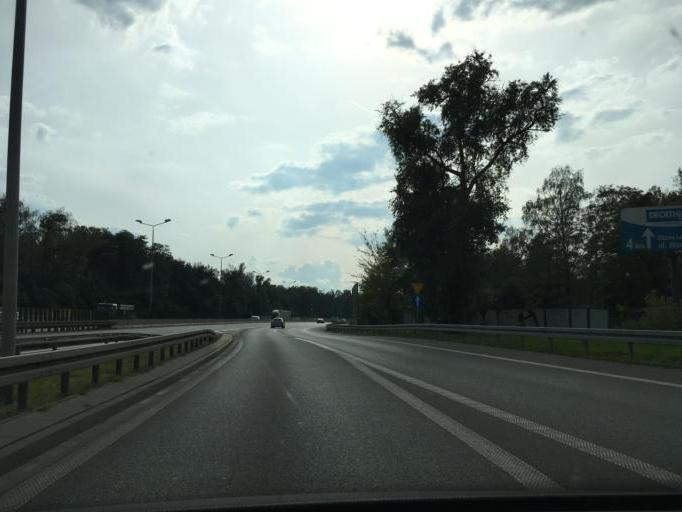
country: PL
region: Masovian Voivodeship
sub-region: Warszawa
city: Bemowo
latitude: 52.2540
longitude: 20.9451
